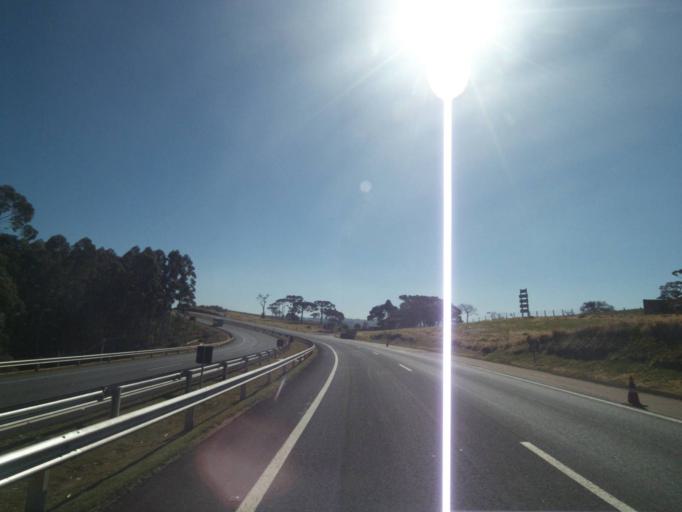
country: BR
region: Parana
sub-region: Carambei
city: Carambei
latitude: -24.9033
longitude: -50.4225
